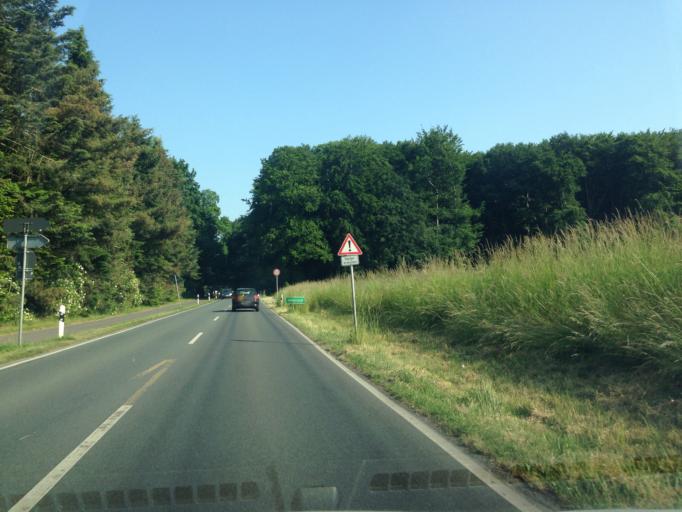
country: DE
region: North Rhine-Westphalia
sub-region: Regierungsbezirk Munster
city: Muenster
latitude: 51.9499
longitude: 7.5574
